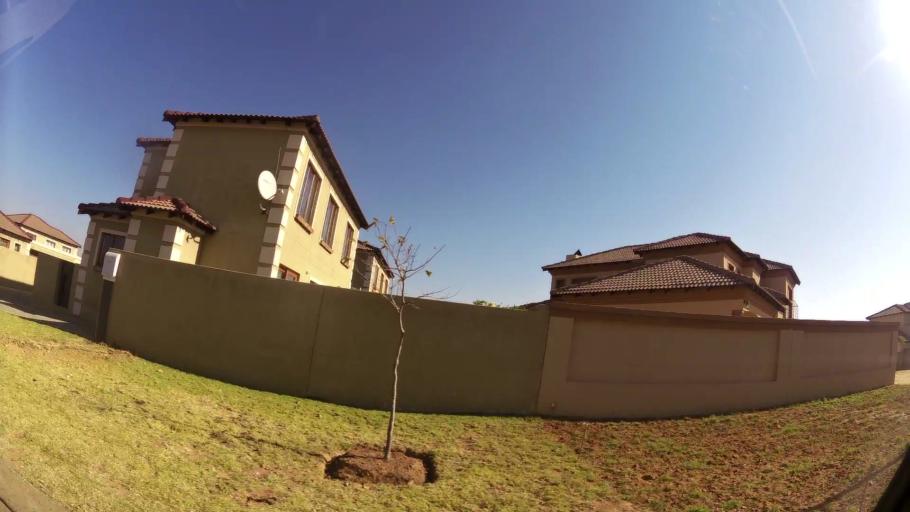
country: ZA
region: Gauteng
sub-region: City of Tshwane Metropolitan Municipality
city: Centurion
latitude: -25.9089
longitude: 28.1308
